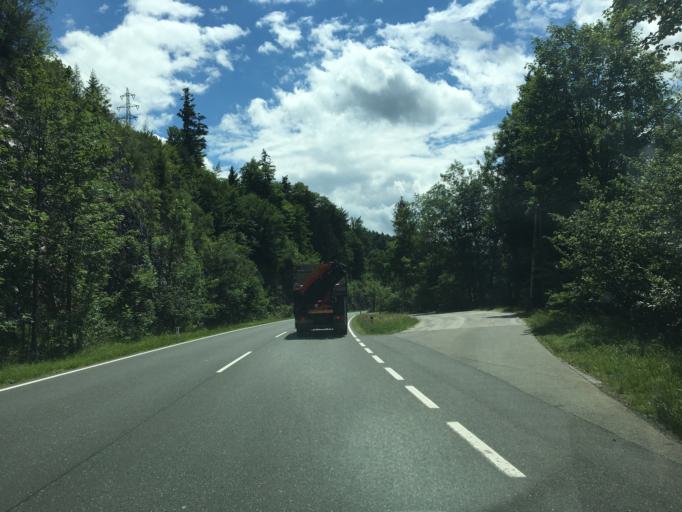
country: AT
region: Salzburg
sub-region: Politischer Bezirk Salzburg-Umgebung
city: Ebenau
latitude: 47.7573
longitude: 13.1799
